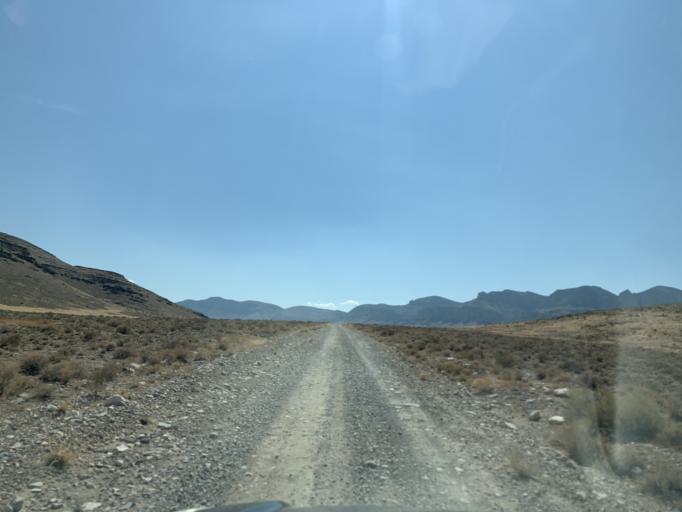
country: US
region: Utah
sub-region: Beaver County
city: Milford
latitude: 38.9780
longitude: -113.4498
